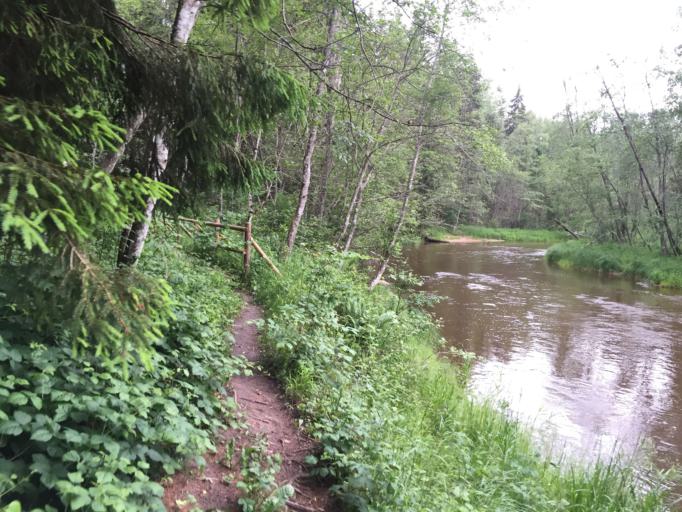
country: LV
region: Ligatne
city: Ligatne
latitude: 57.2351
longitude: 25.1552
